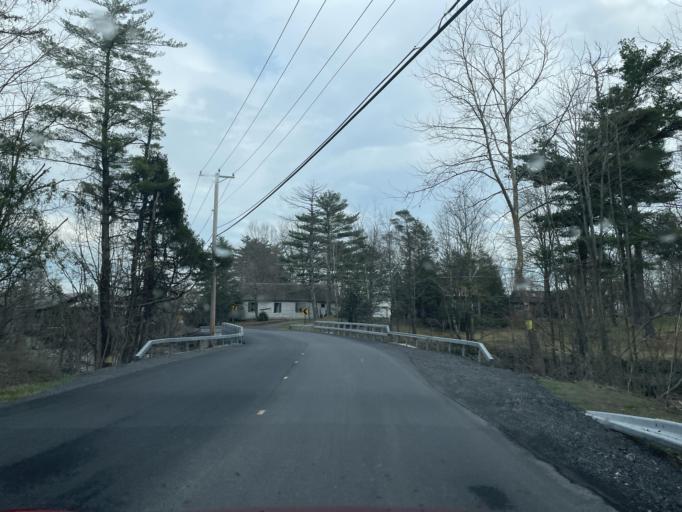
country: US
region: New York
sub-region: Ulster County
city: Manorville
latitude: 42.1130
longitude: -74.0494
